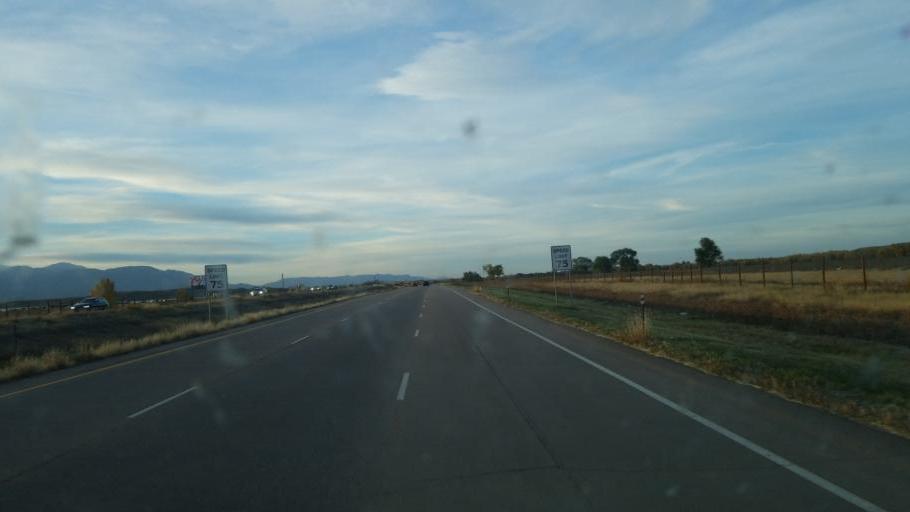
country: US
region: Colorado
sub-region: El Paso County
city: Fountain
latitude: 38.5943
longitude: -104.6732
